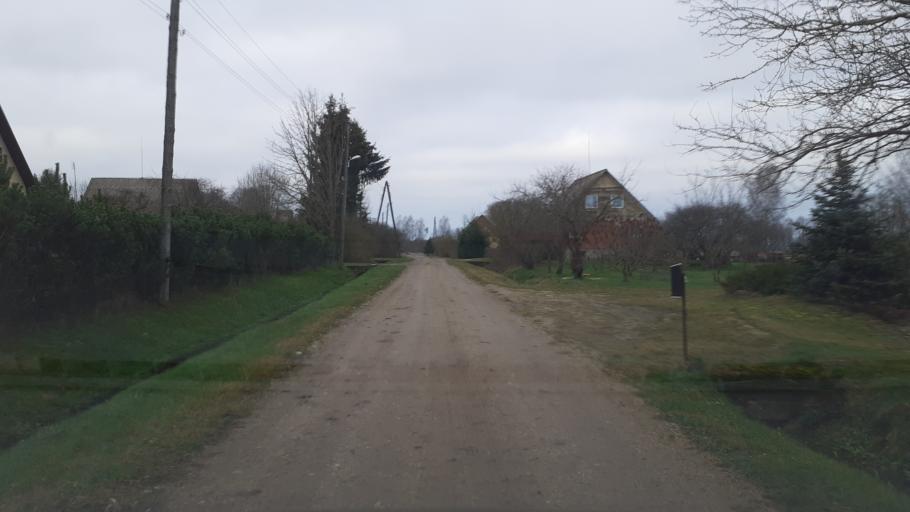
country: LV
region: Aizpute
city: Aizpute
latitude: 56.8020
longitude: 21.6697
